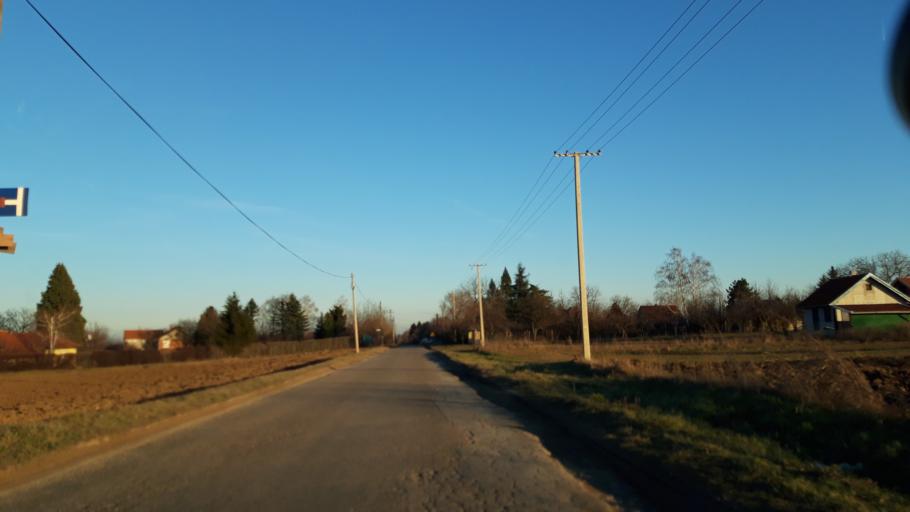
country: RS
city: Cortanovci
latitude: 45.1596
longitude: 19.9989
